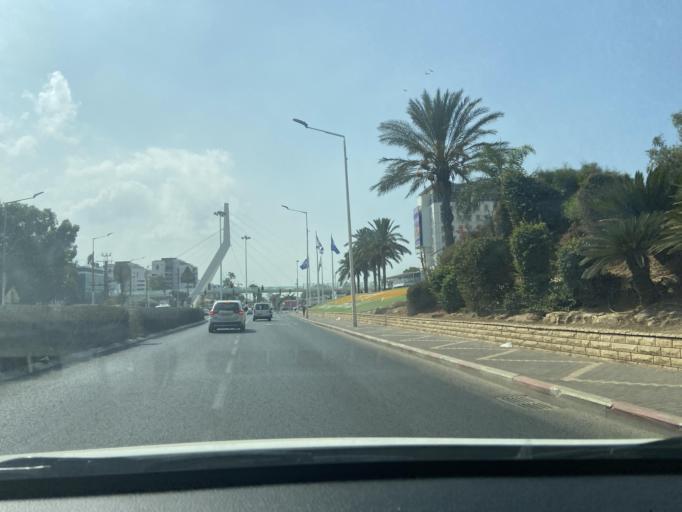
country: IL
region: Northern District
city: Nahariya
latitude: 33.0072
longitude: 35.0996
